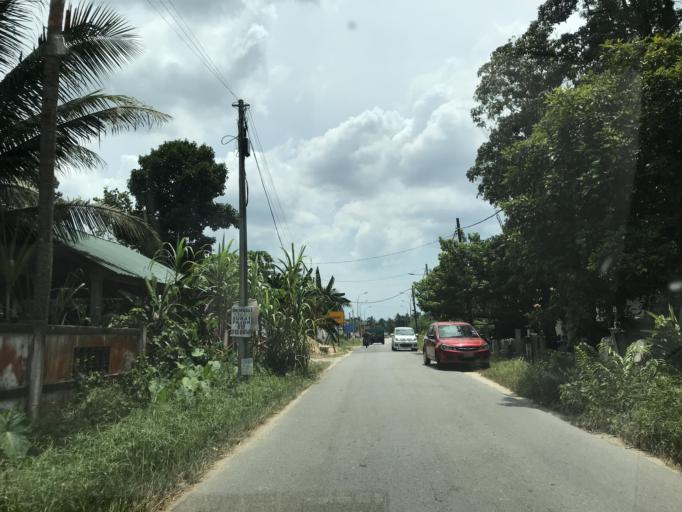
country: MY
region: Kelantan
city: Kota Bharu
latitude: 6.1430
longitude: 102.1863
